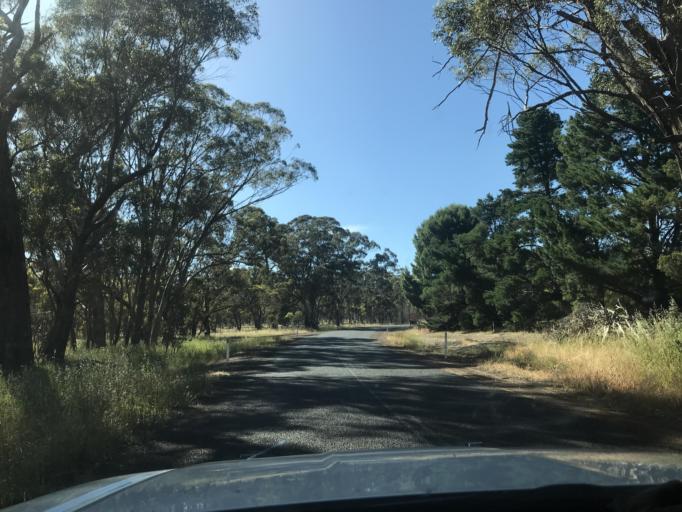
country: AU
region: Victoria
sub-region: Horsham
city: Horsham
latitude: -37.0929
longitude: 141.7729
